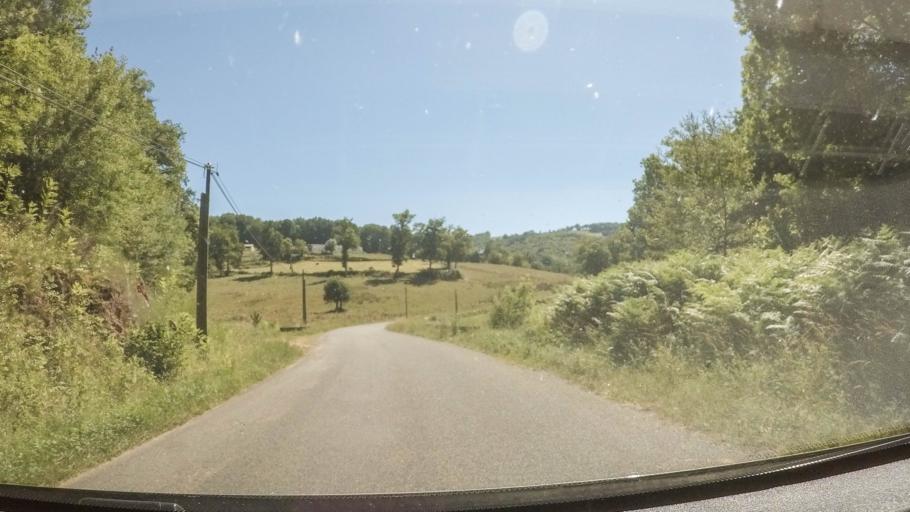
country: FR
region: Midi-Pyrenees
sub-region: Departement de l'Aveyron
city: Firmi
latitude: 44.4795
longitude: 2.3410
